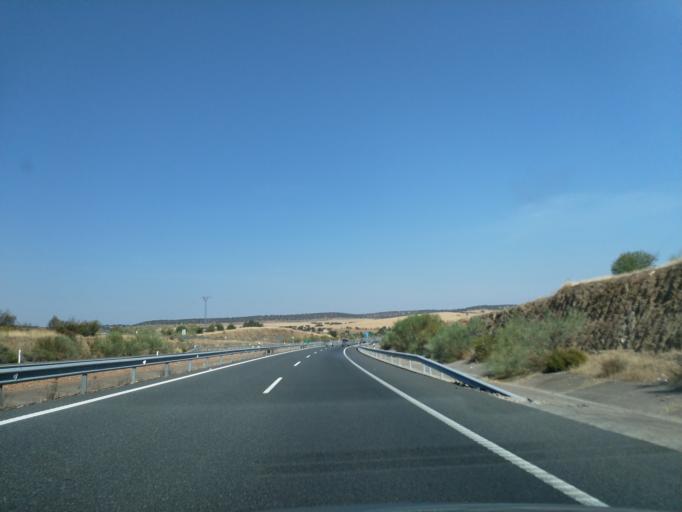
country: ES
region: Extremadura
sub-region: Provincia de Badajoz
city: Aljucen
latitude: 39.0403
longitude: -6.3386
